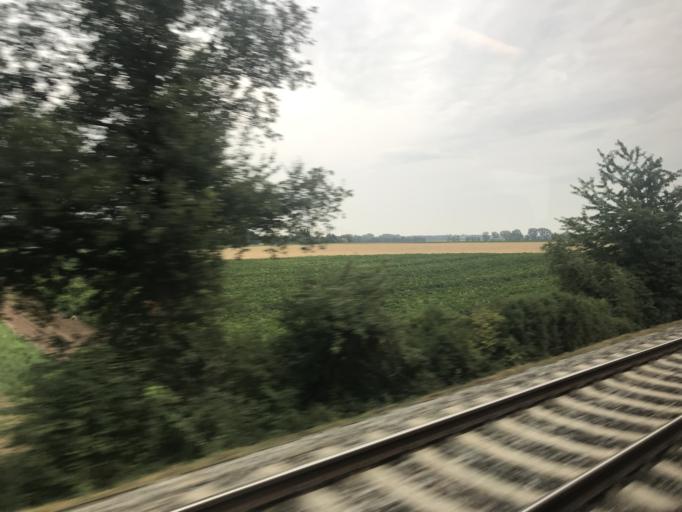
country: DE
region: Bavaria
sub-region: Regierungsbezirk Unterfranken
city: Bergtheim
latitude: 49.9099
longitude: 10.0821
